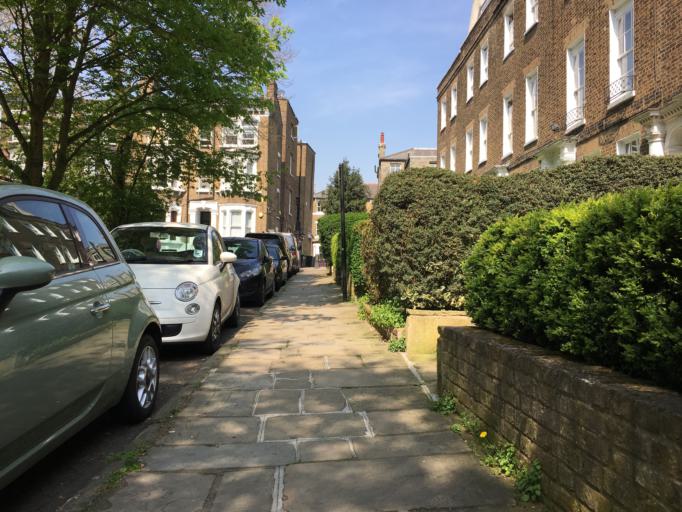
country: GB
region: England
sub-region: Greater London
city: Camden Town
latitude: 51.5583
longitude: -0.1478
